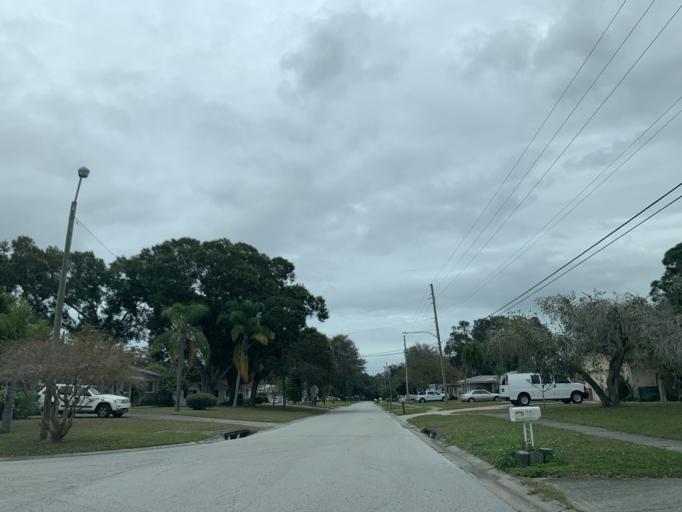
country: US
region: Florida
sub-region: Pinellas County
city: Belleair
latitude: 27.9351
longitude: -82.7828
